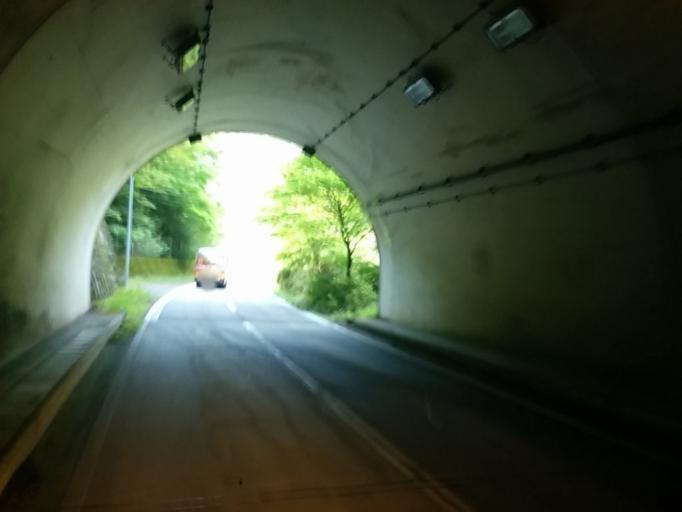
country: JP
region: Ehime
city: Niihama
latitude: 33.8801
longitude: 133.2972
